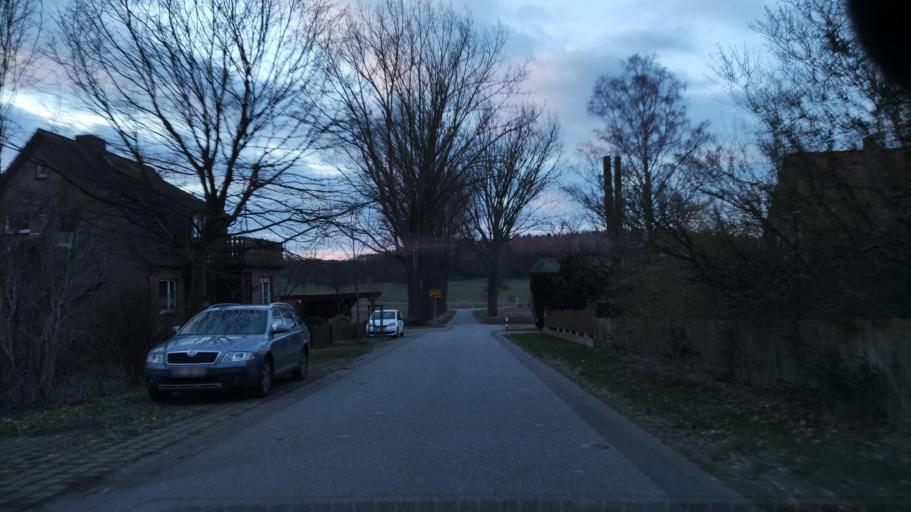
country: DE
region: Lower Saxony
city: Natendorf
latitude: 53.0736
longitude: 10.4432
